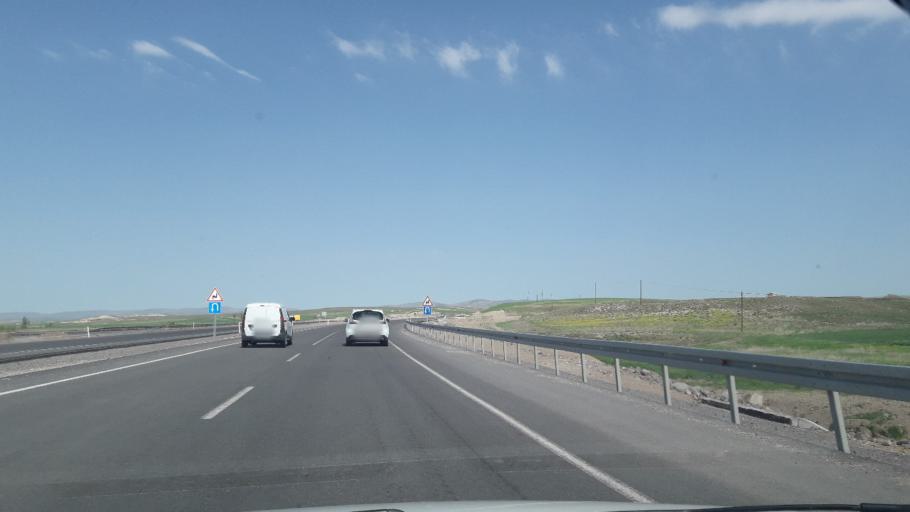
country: TR
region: Sivas
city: Deliktas
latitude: 39.2083
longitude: 37.2048
